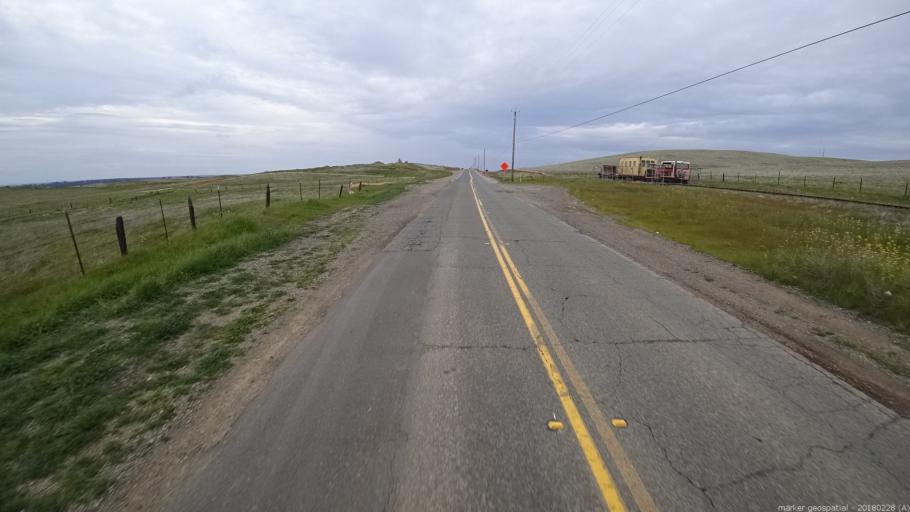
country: US
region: California
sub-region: El Dorado County
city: El Dorado Hills
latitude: 38.6285
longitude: -121.0944
